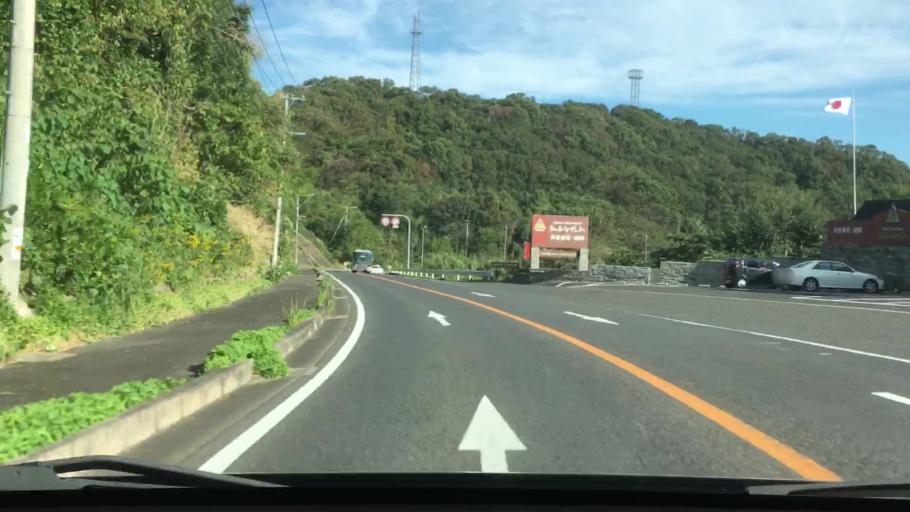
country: JP
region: Nagasaki
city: Sasebo
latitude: 33.0903
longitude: 129.7567
